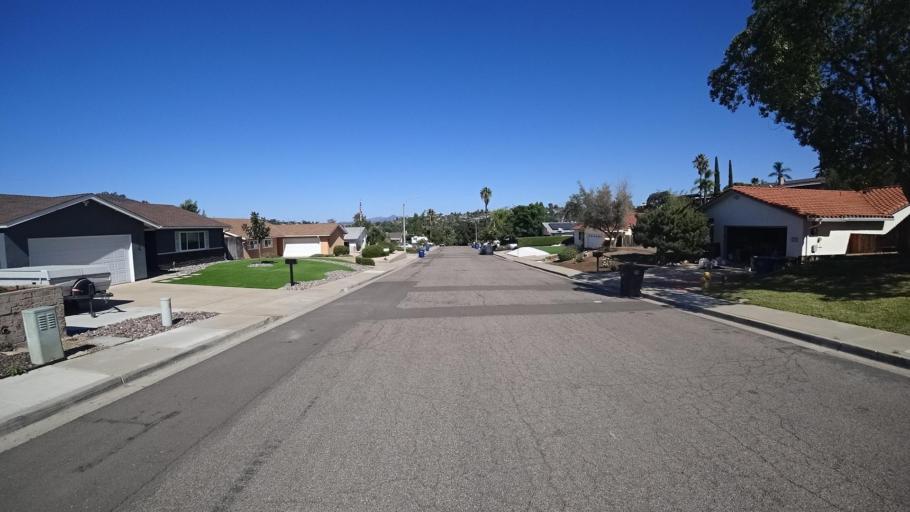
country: US
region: California
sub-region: San Diego County
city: Bostonia
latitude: 32.8178
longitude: -116.9276
